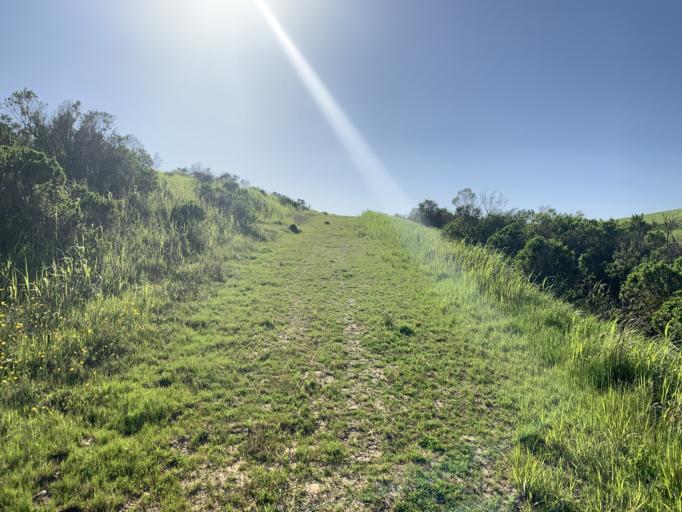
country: US
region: California
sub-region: Contra Costa County
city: Martinez
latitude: 38.0115
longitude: -122.1511
